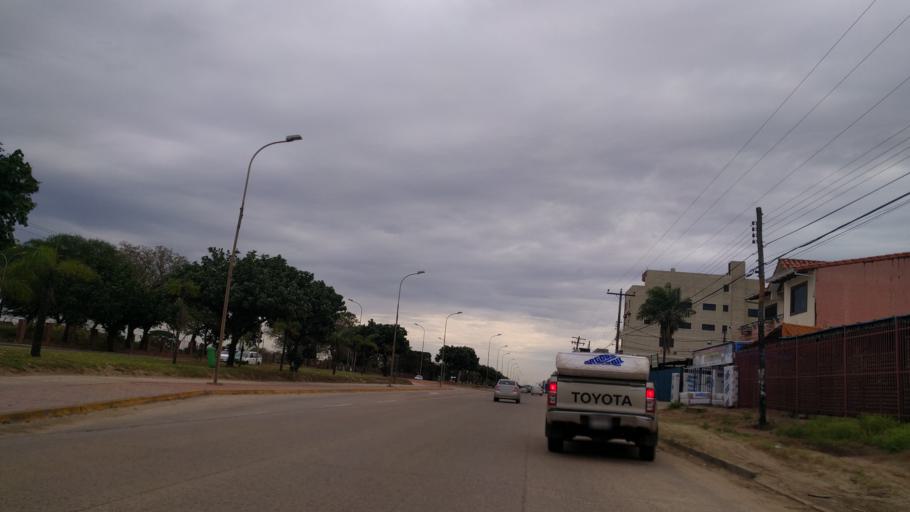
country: BO
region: Santa Cruz
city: Santa Cruz de la Sierra
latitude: -17.8310
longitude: -63.1854
